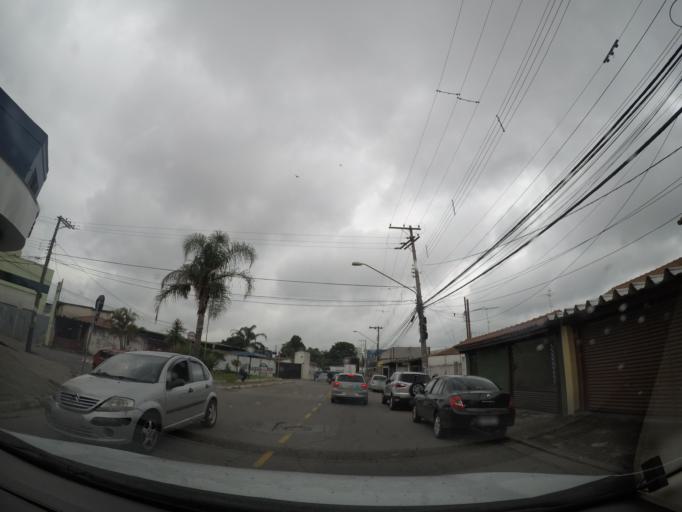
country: BR
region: Sao Paulo
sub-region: Guarulhos
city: Guarulhos
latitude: -23.4328
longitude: -46.5054
